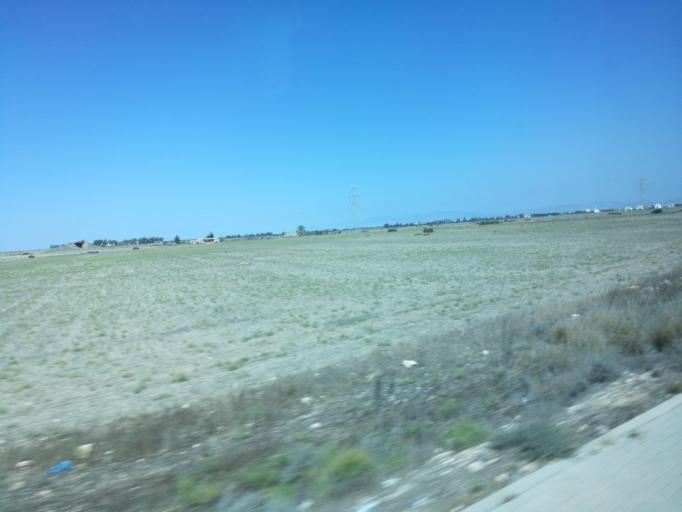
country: CY
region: Ammochostos
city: Famagusta
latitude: 35.1759
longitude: 33.8971
